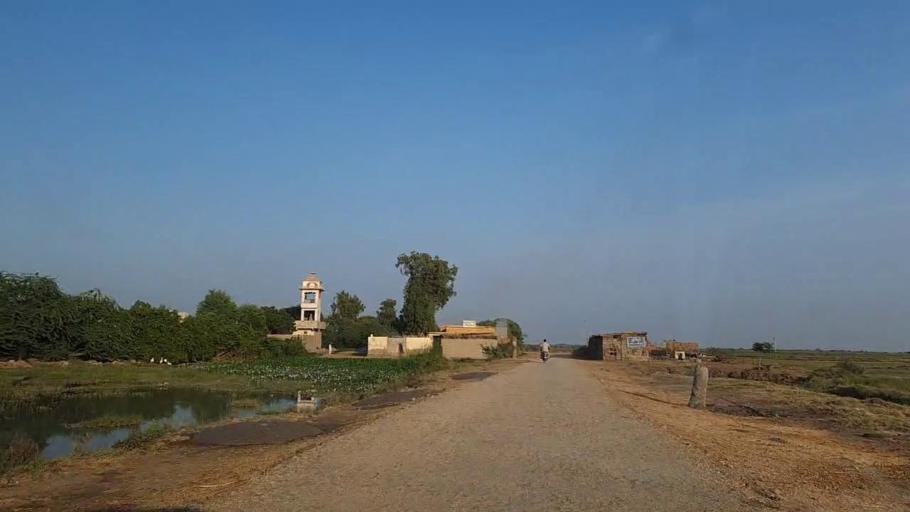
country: PK
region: Sindh
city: Mirpur Batoro
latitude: 24.6075
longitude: 68.0985
